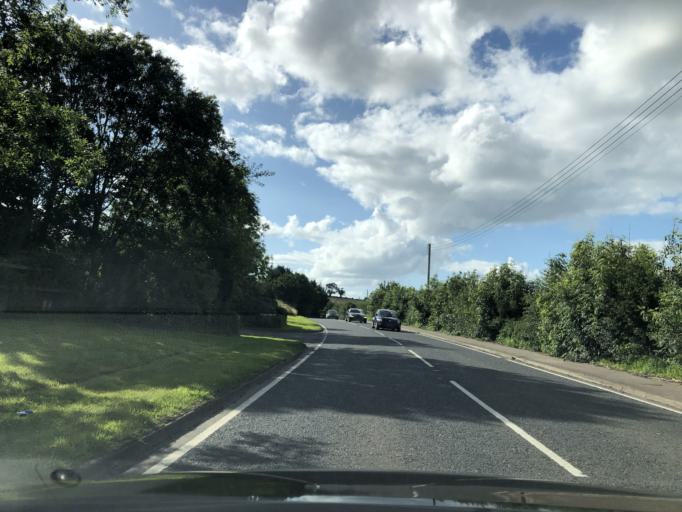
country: GB
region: Northern Ireland
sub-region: Castlereagh District
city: Dundonald
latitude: 54.5781
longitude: -5.7880
